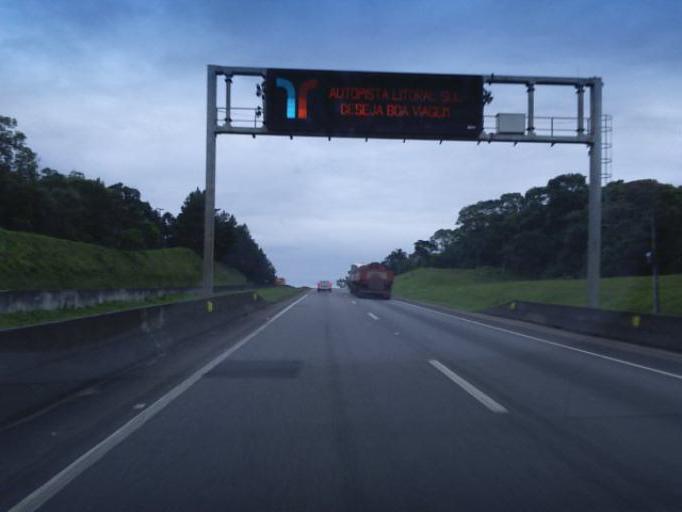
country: BR
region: Parana
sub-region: Sao Jose Dos Pinhais
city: Sao Jose dos Pinhais
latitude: -25.7968
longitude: -49.1305
